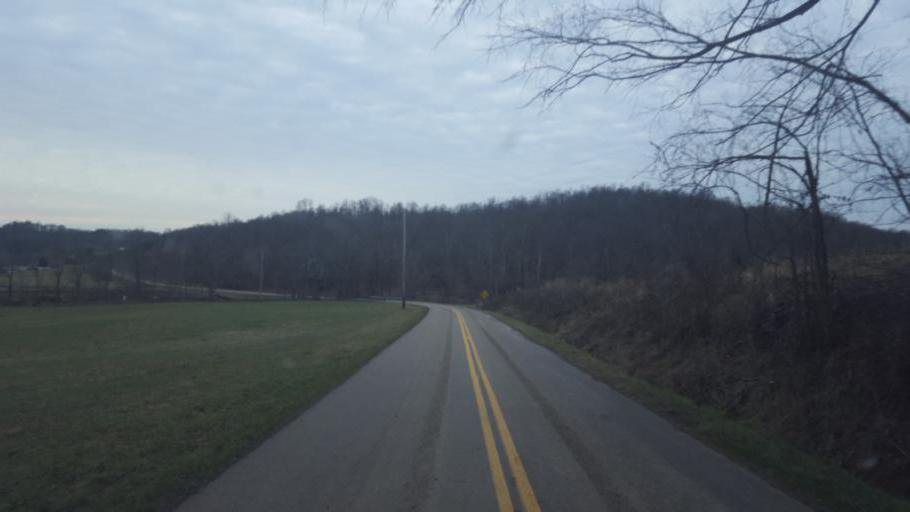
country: US
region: Ohio
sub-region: Gallia County
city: Gallipolis
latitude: 38.7290
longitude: -82.3215
